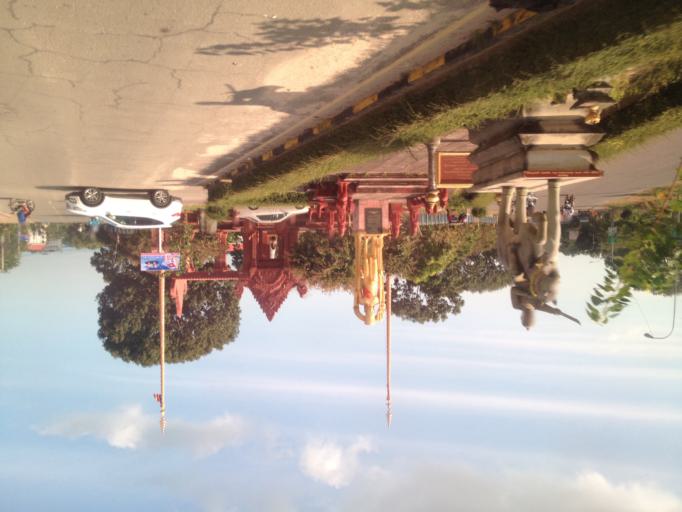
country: KH
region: Preah Sihanouk
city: Sihanoukville
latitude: 10.6320
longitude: 103.5078
